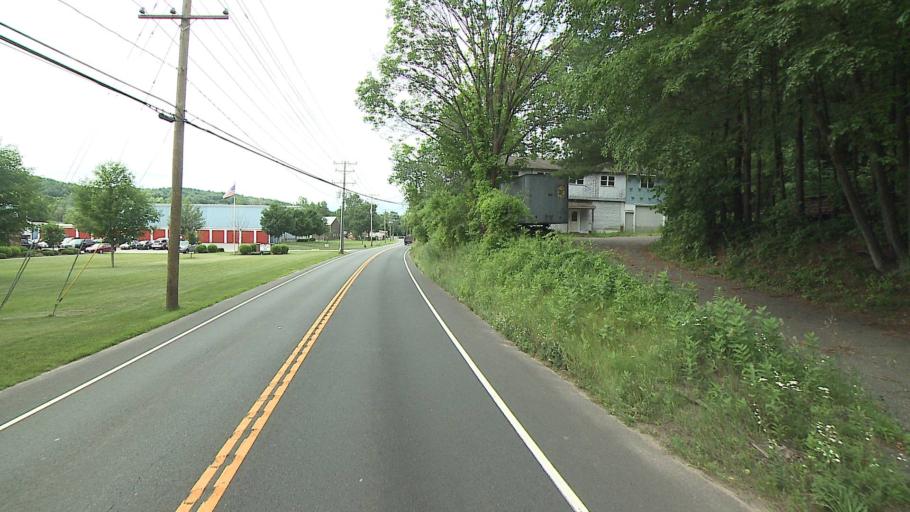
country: US
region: Connecticut
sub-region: Litchfield County
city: Winsted
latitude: 41.9143
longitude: -73.0639
